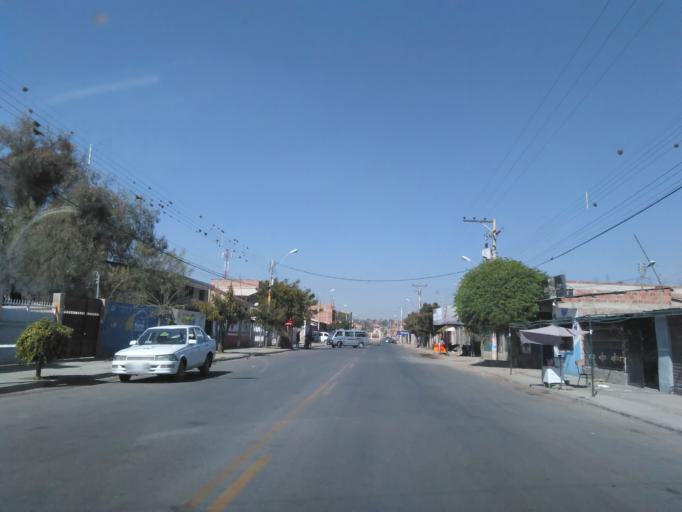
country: BO
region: Cochabamba
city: Sipe Sipe
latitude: -17.4086
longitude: -66.2822
